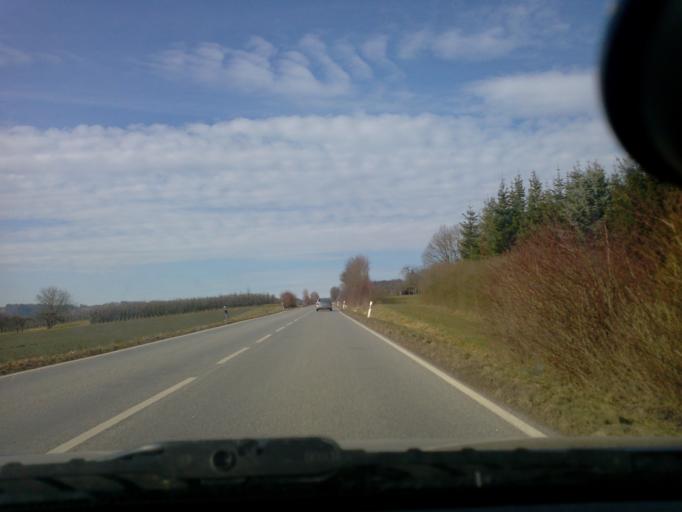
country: DE
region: Baden-Wuerttemberg
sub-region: Regierungsbezirk Stuttgart
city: Brackenheim
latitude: 49.0919
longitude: 9.0474
